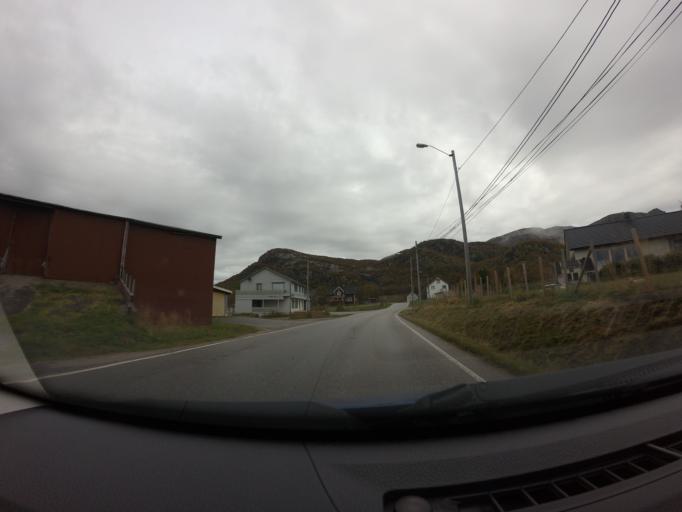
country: NO
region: Vest-Agder
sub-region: Sirdal
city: Tonstad
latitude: 58.9563
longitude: 6.9286
